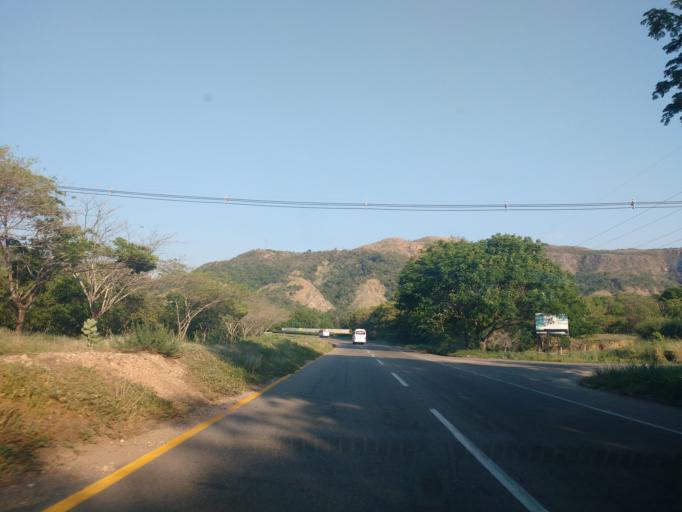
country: CO
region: Cundinamarca
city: Ricaurte
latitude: 4.2490
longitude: -74.7680
